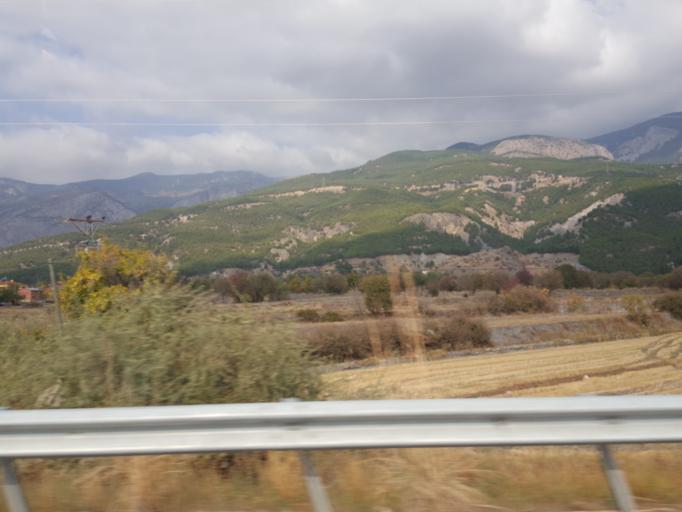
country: TR
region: Corum
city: Kargi
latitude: 41.1318
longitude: 34.4298
